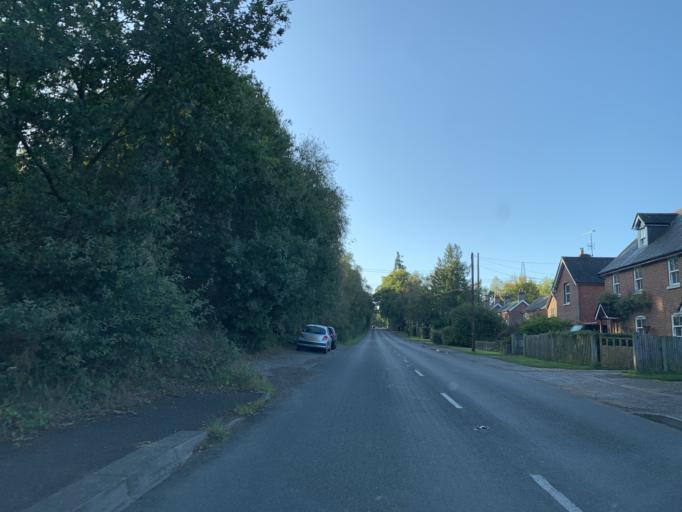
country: GB
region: England
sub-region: Wiltshire
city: Whiteparish
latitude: 50.9661
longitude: -1.6341
